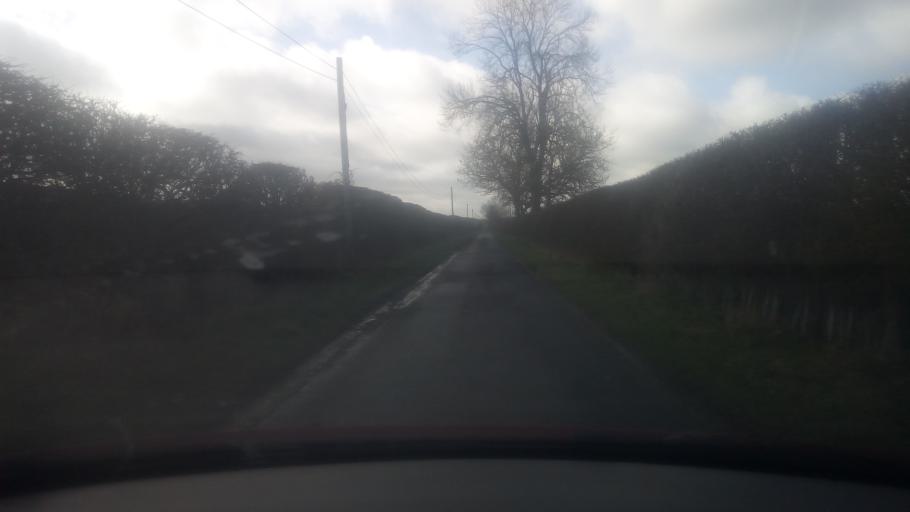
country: GB
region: Scotland
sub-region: The Scottish Borders
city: Saint Boswells
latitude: 55.5272
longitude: -2.6499
